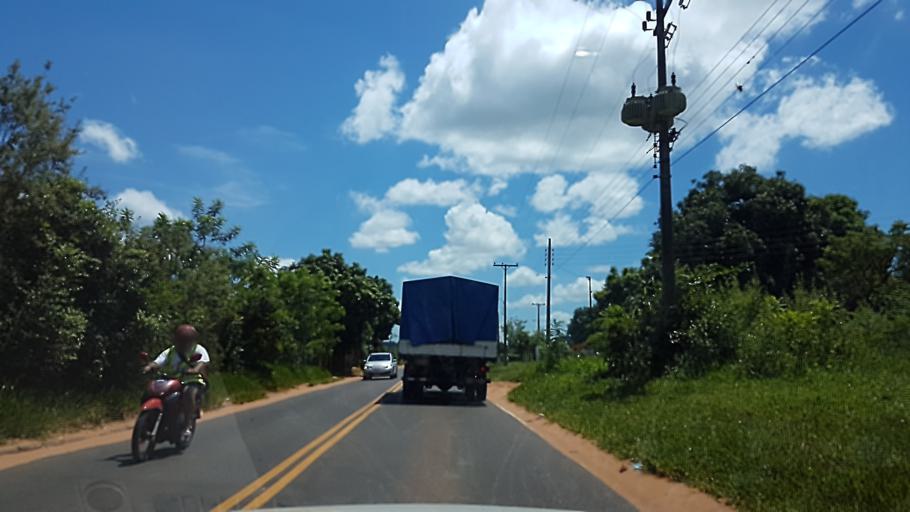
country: PY
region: Central
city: Capiata
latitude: -25.3197
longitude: -57.4536
